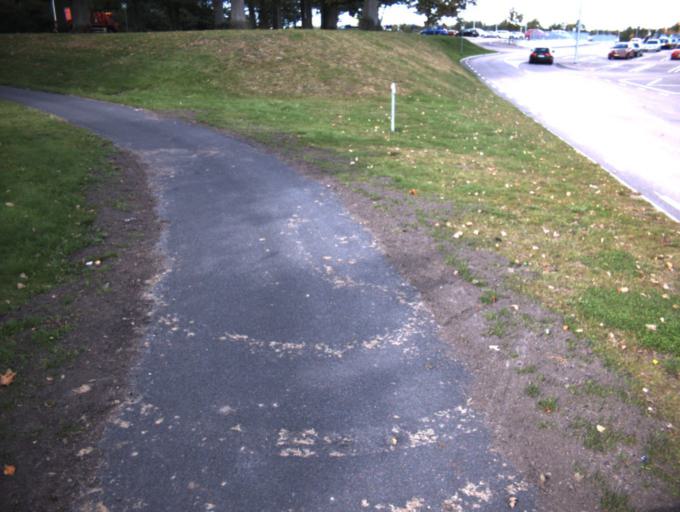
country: SE
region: Skane
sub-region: Helsingborg
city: Odakra
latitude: 56.0900
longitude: 12.7542
